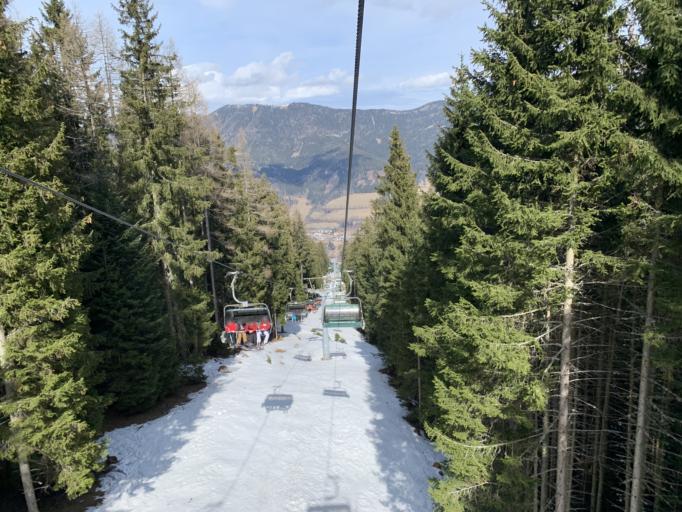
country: AT
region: Styria
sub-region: Politischer Bezirk Bruck-Muerzzuschlag
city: Spital am Semmering
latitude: 47.5941
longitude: 15.7635
